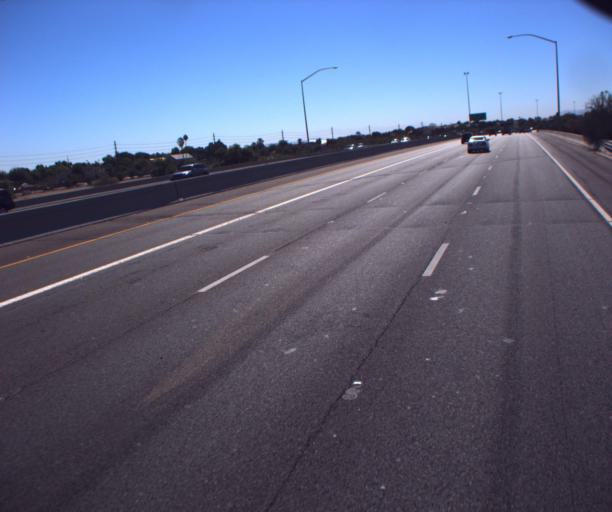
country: US
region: Arizona
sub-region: Maricopa County
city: Sun City
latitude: 33.6220
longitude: -112.2399
